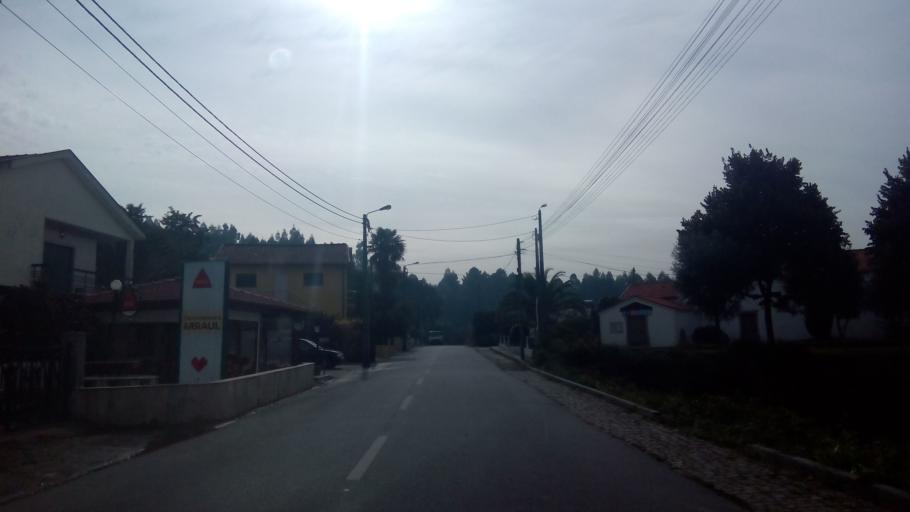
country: PT
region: Porto
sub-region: Paredes
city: Gandra
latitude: 41.1896
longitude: -8.4268
